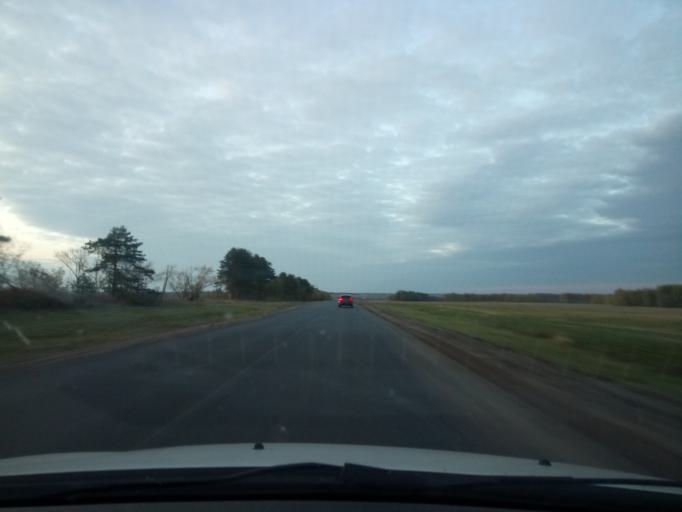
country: RU
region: Nizjnij Novgorod
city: Bol'shoye Murashkino
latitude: 55.8597
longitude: 44.7486
